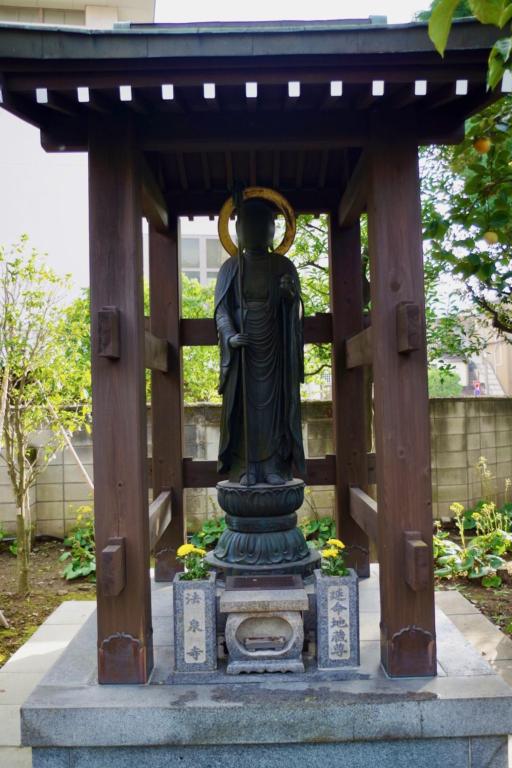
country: JP
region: Tokyo
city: Urayasu
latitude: 35.7260
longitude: 139.8140
